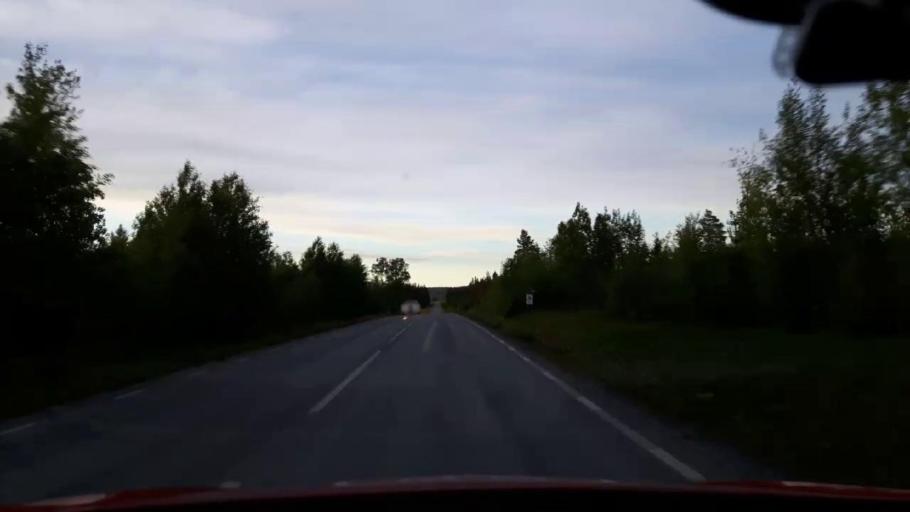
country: SE
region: Jaemtland
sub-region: OEstersunds Kommun
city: Ostersund
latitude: 63.1422
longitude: 14.4713
